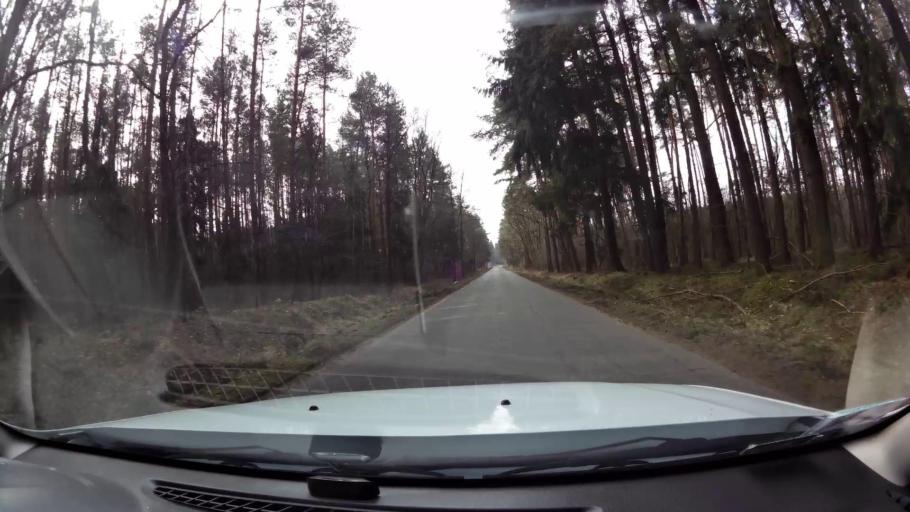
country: PL
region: West Pomeranian Voivodeship
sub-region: Powiat mysliborski
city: Debno
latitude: 52.8147
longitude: 14.6360
